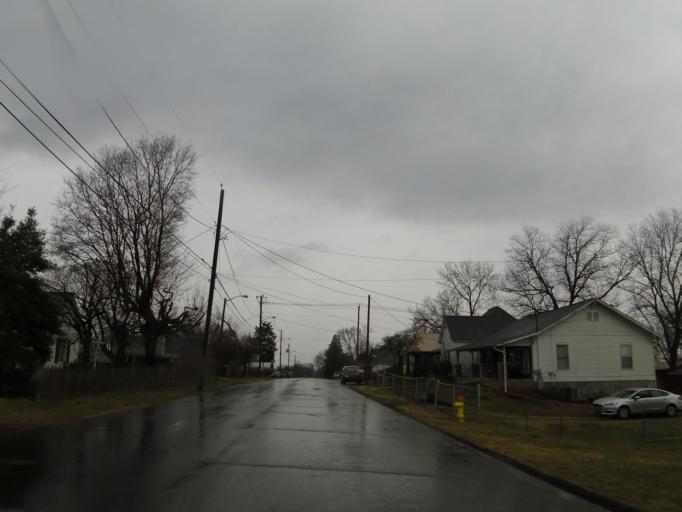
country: US
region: Tennessee
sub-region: Knox County
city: Knoxville
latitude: 35.9789
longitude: -83.9489
